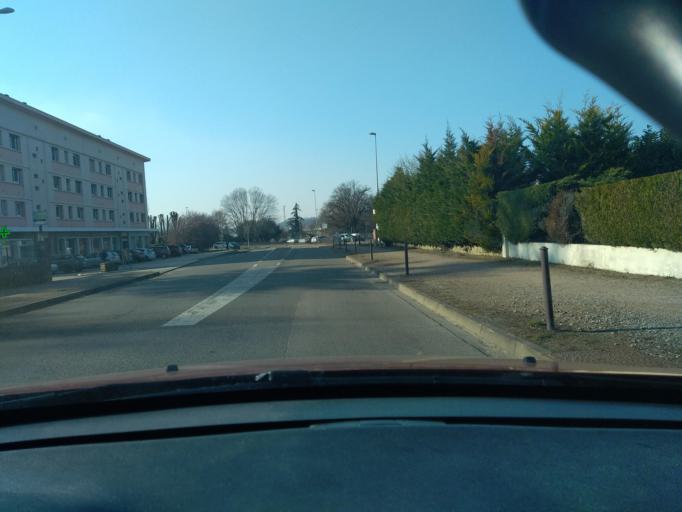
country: FR
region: Franche-Comte
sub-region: Departement du Jura
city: Perrigny
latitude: 46.6689
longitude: 5.5755
